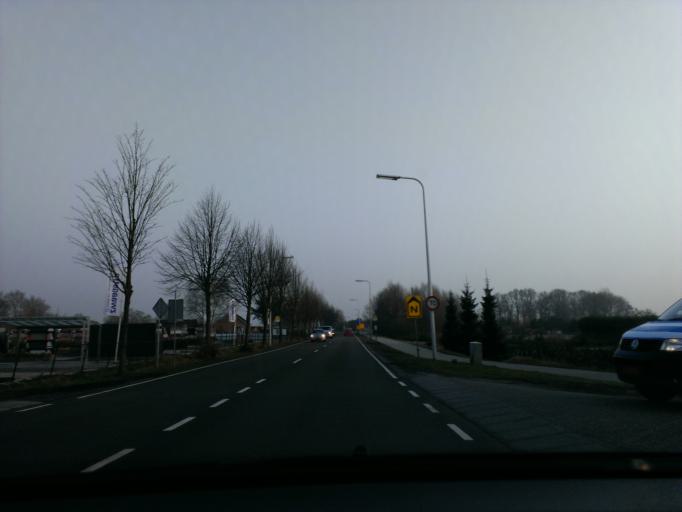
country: NL
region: Drenthe
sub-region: Gemeente Hoogeveen
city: Hoogeveen
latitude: 52.7188
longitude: 6.5189
